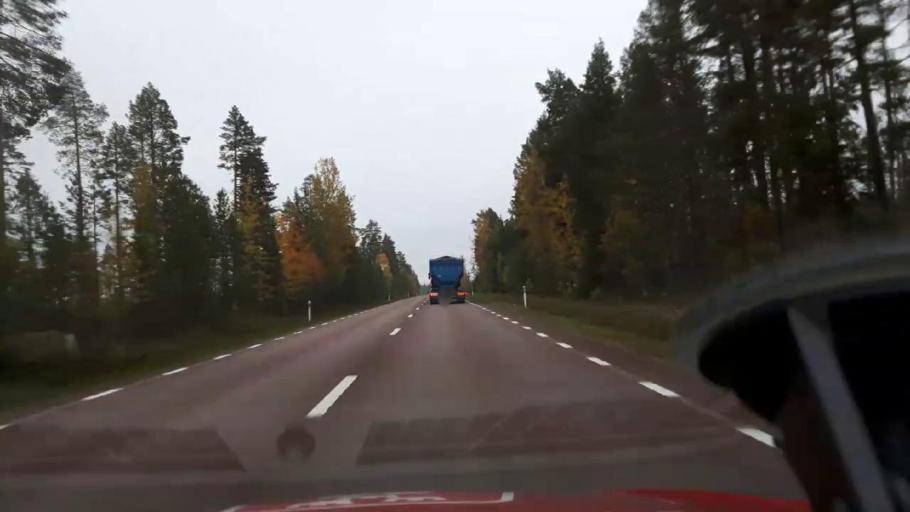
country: SE
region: Jaemtland
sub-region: Bergs Kommun
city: Hoverberg
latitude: 62.5976
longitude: 14.4207
